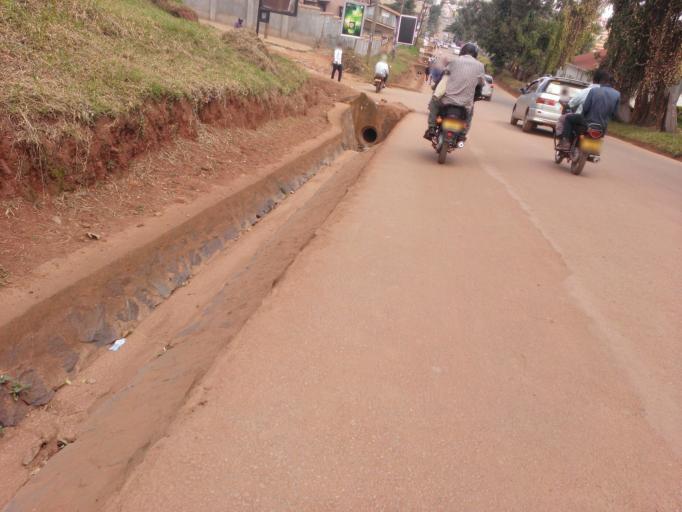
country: UG
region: Central Region
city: Kampala Central Division
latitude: 0.3255
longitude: 32.5699
